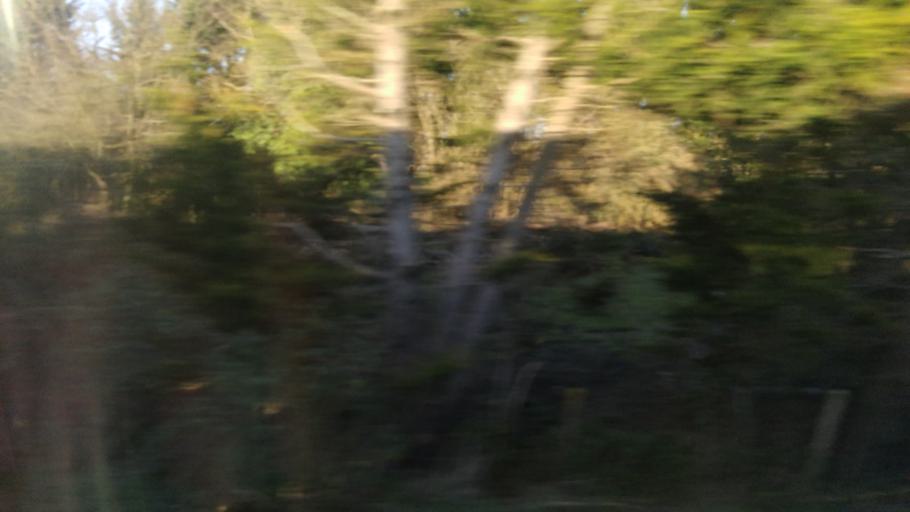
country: GB
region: England
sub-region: Kent
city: Marden
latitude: 51.1739
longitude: 0.5158
